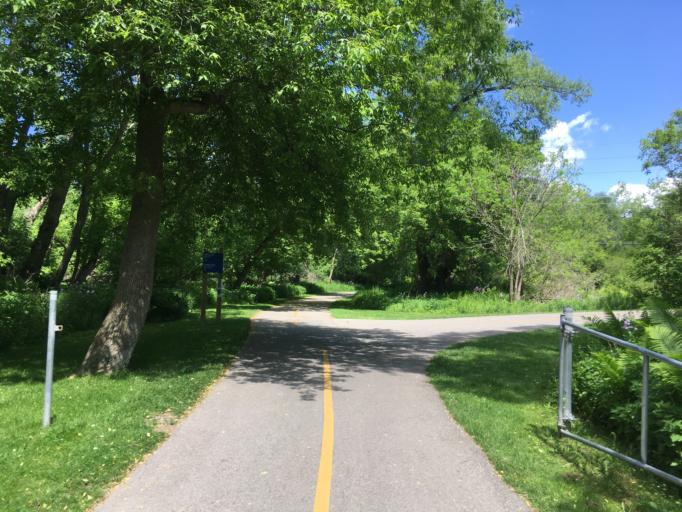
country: CA
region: Ontario
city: Oshawa
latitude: 43.8661
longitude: -78.8401
